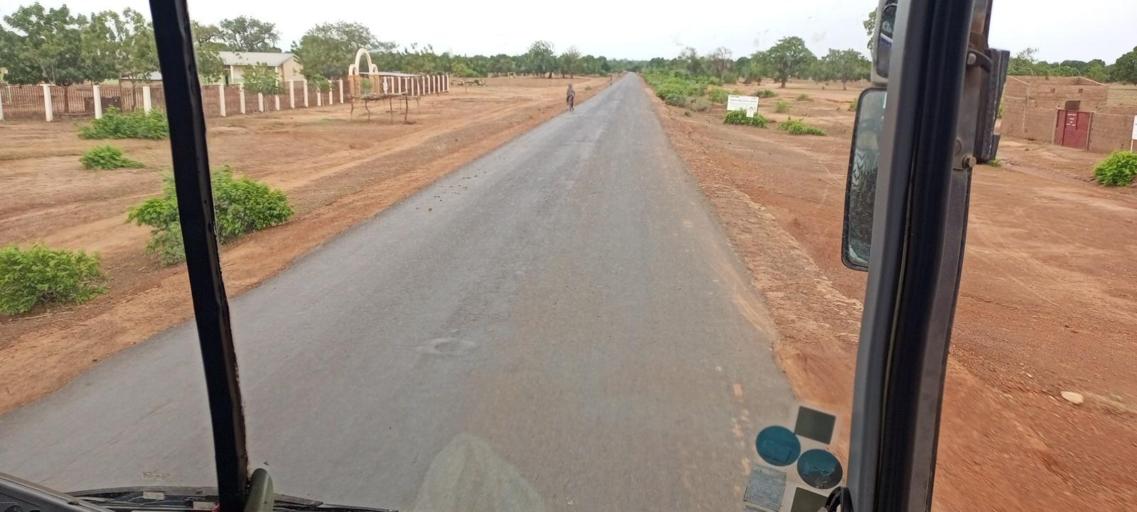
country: ML
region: Segou
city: Bla
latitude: 12.6868
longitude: -5.7237
